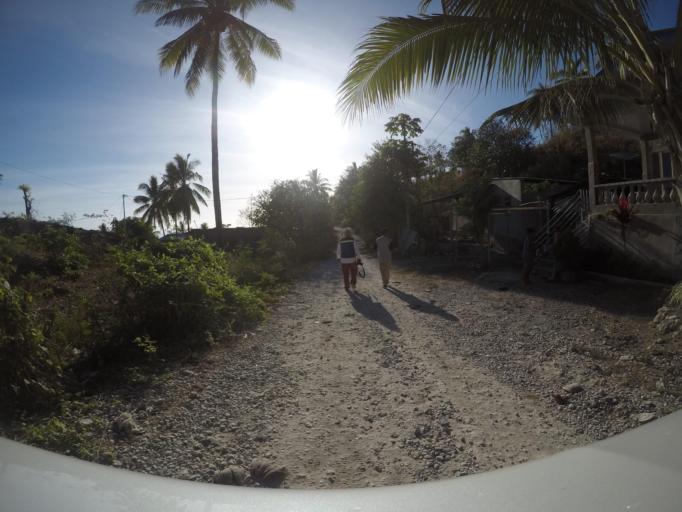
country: TL
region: Baucau
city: Baucau
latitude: -8.4636
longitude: 126.4623
